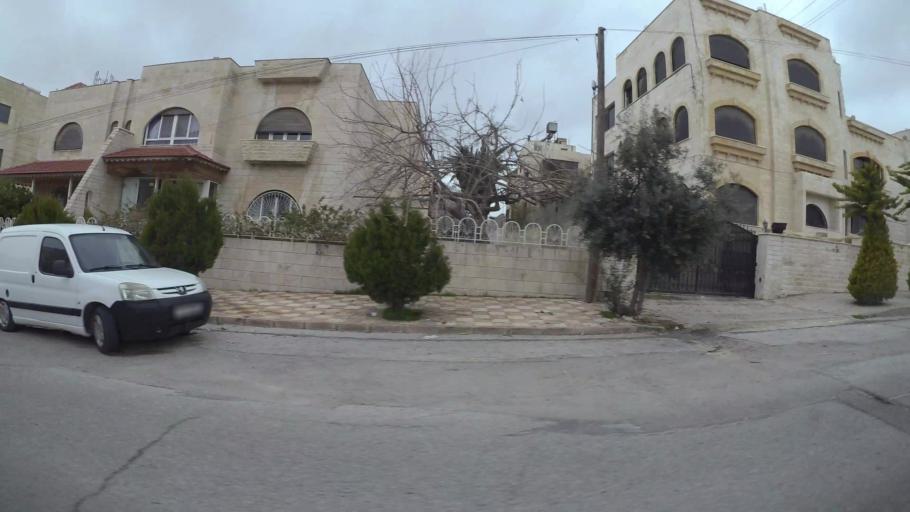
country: JO
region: Amman
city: Al Jubayhah
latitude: 31.9958
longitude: 35.8433
